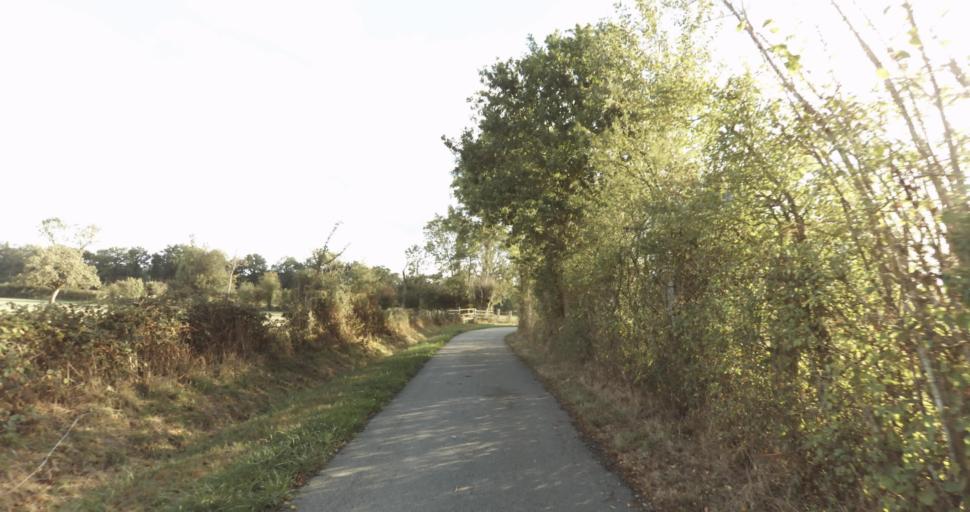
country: FR
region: Lower Normandy
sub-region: Departement de l'Orne
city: Sainte-Gauburge-Sainte-Colombe
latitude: 48.7263
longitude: 0.4081
